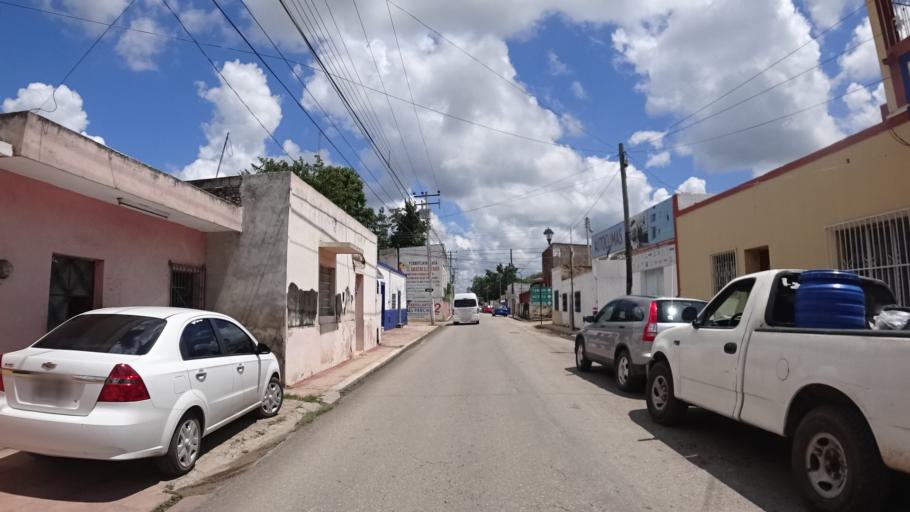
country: MX
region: Yucatan
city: Valladolid
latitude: 20.6899
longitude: -88.2105
